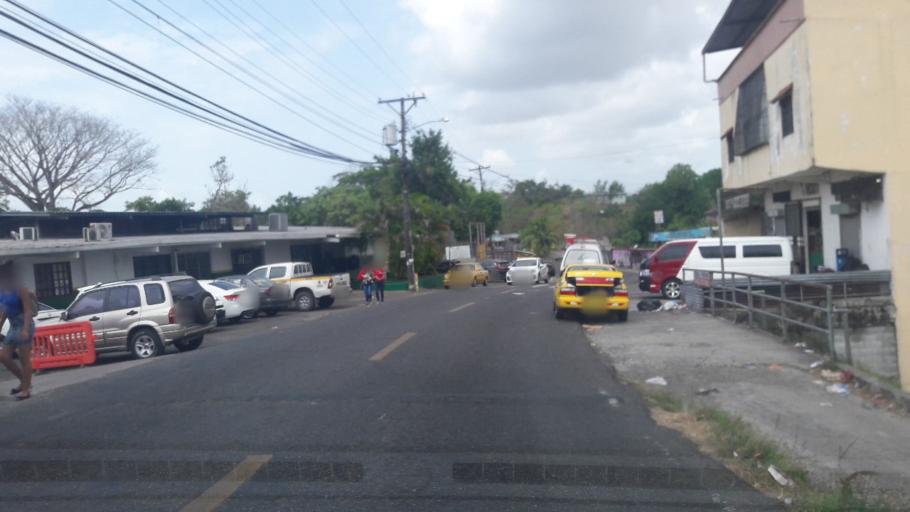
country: PA
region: Panama
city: Alcalde Diaz
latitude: 9.1123
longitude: -79.5557
